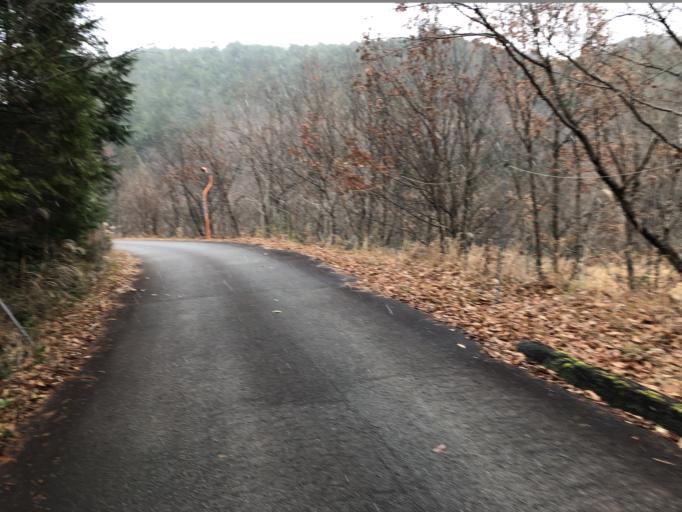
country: JP
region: Kyoto
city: Kameoka
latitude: 35.0610
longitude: 135.4934
